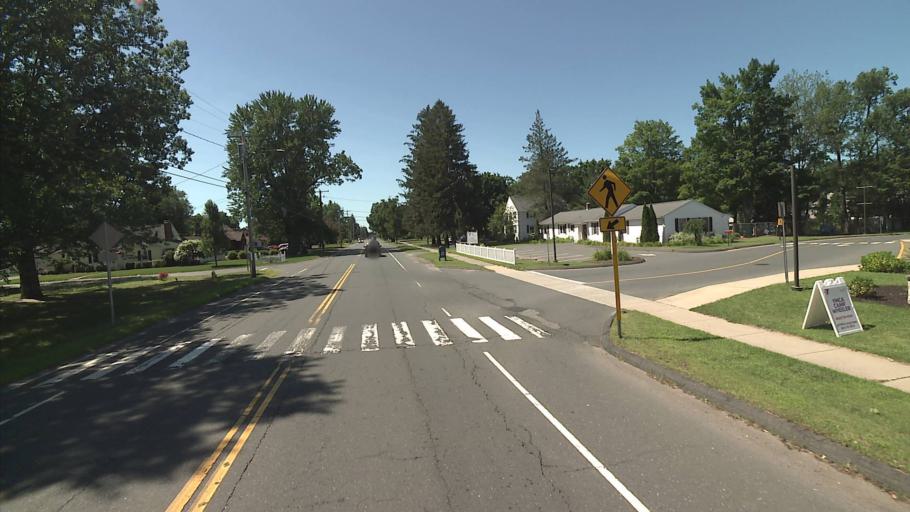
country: US
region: Connecticut
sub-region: Hartford County
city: Plainville
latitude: 41.6816
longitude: -72.8550
